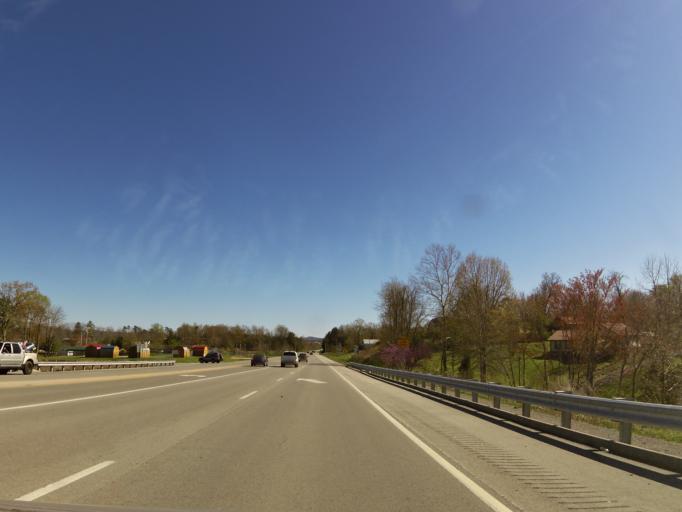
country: US
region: Kentucky
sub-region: McCreary County
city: Pine Knot
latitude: 36.6584
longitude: -84.4380
